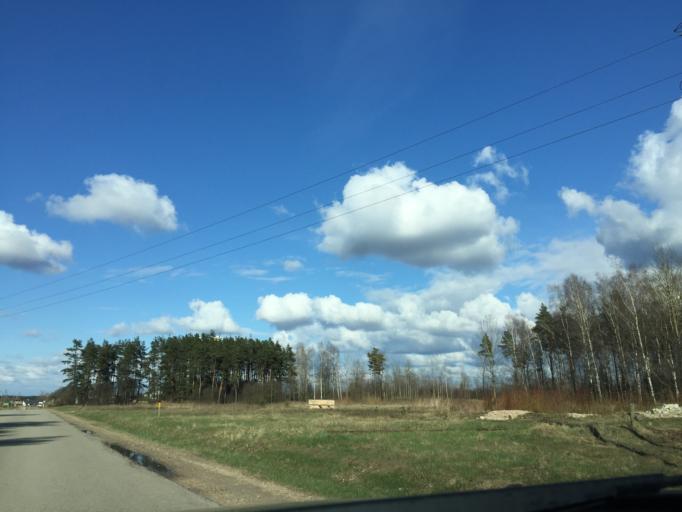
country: LV
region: Kekava
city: Kekava
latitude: 56.8343
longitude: 24.2049
